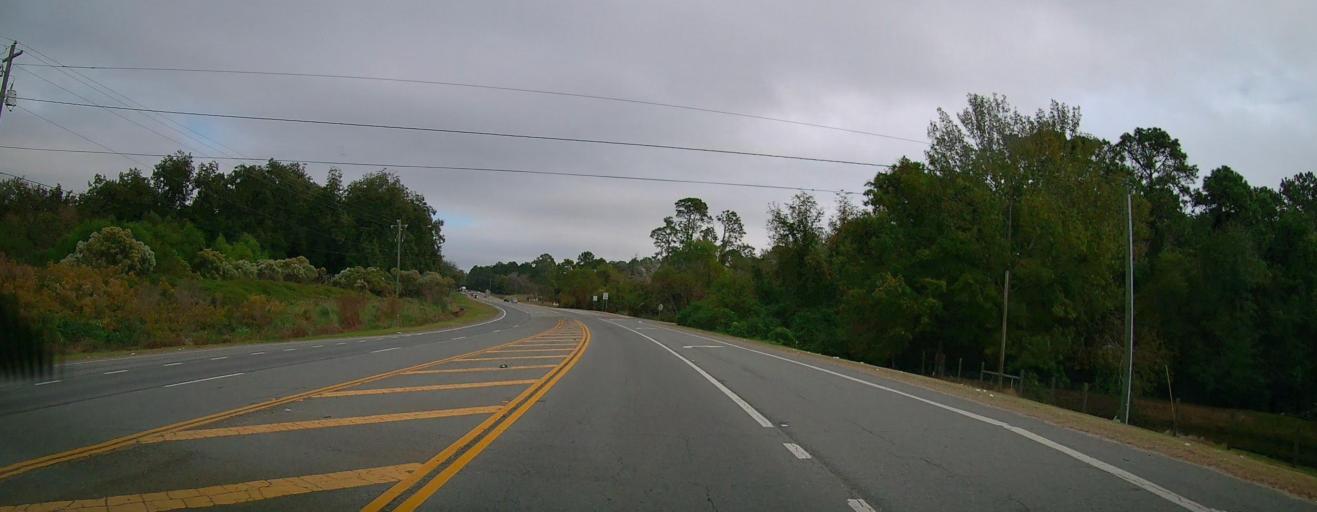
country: US
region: Georgia
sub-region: Tift County
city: Omega
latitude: 31.3338
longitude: -83.6063
